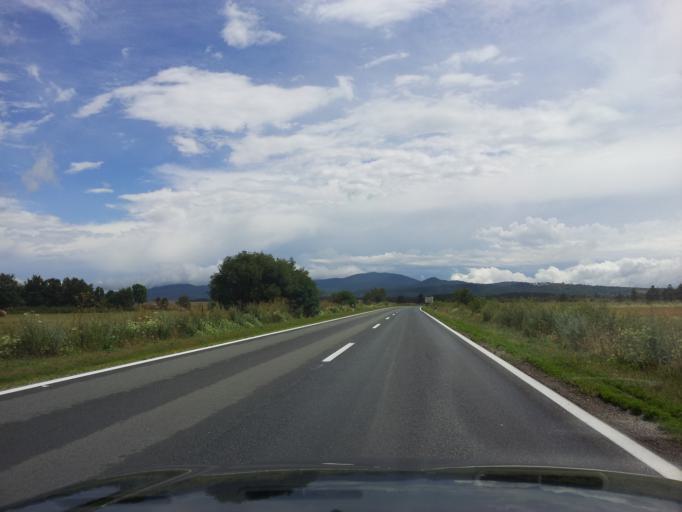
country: BA
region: Federation of Bosnia and Herzegovina
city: Bihac
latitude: 44.5728
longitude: 15.7517
